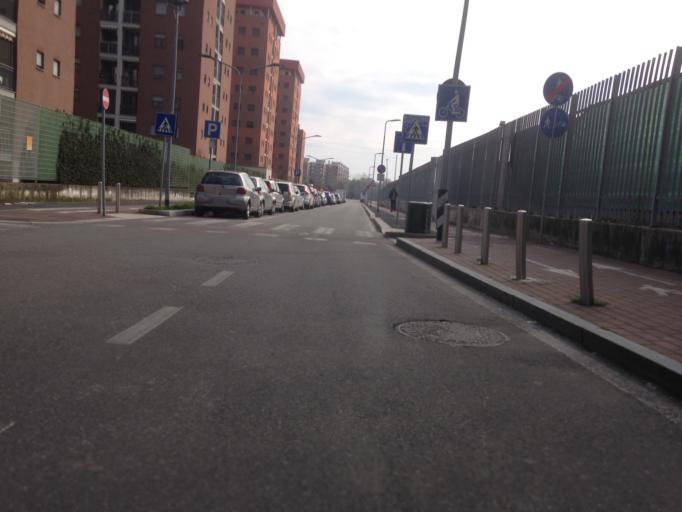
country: IT
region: Lombardy
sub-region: Citta metropolitana di Milano
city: Rozzano
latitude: 45.4244
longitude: 9.1734
